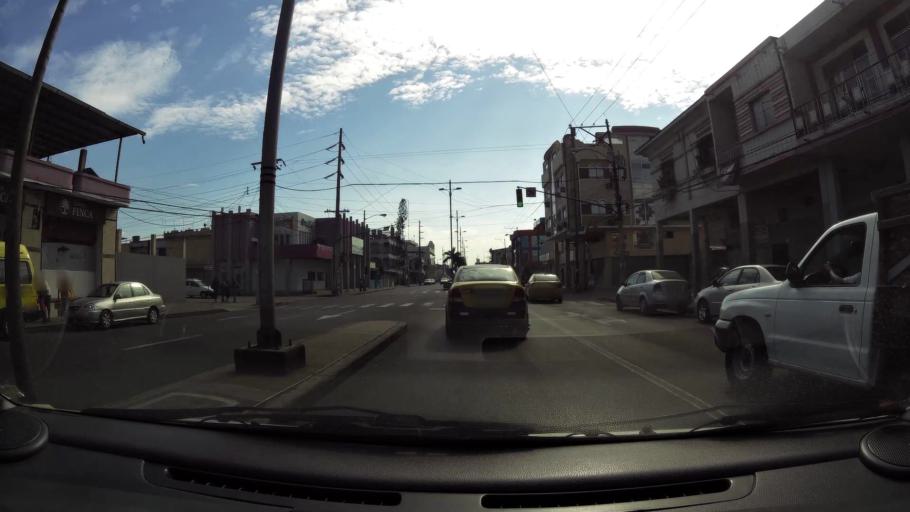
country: EC
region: Guayas
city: Guayaquil
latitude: -2.2024
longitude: -79.9135
